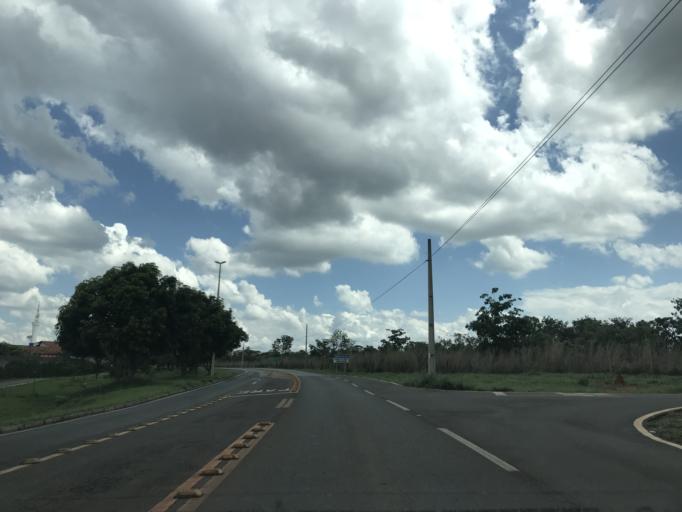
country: BR
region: Federal District
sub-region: Brasilia
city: Brasilia
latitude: -15.6851
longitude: -47.8377
